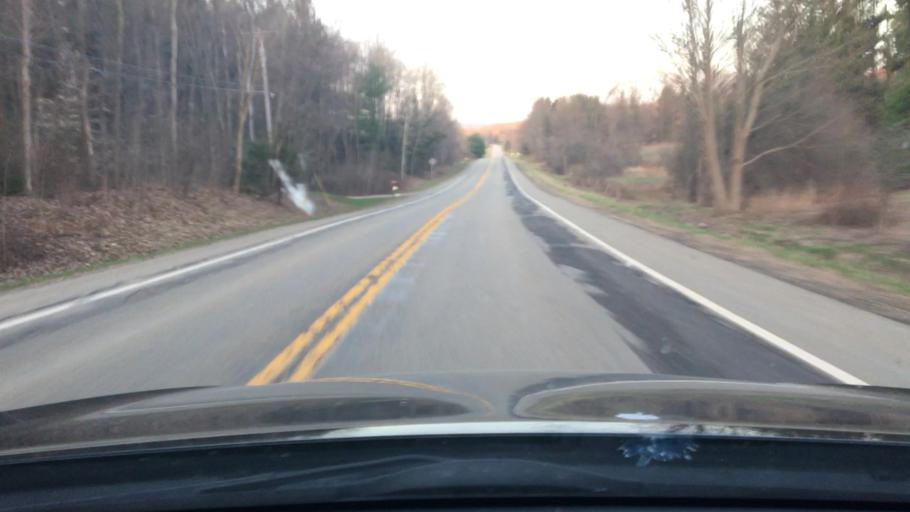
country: US
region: New York
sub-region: Cattaraugus County
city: Randolph
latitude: 42.1847
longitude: -78.9175
